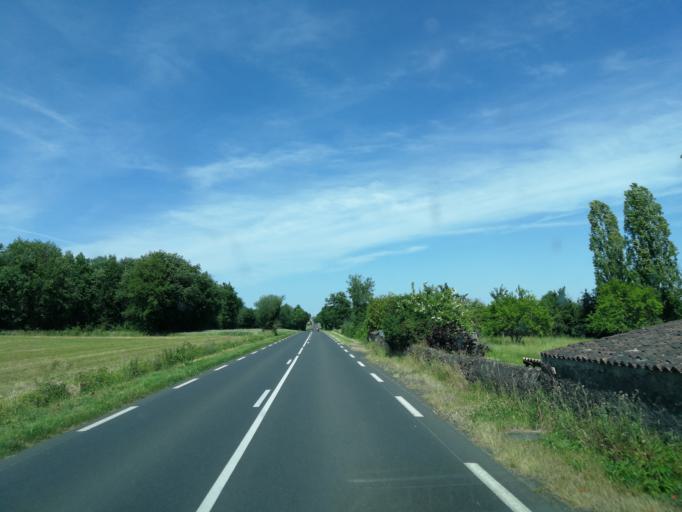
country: FR
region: Poitou-Charentes
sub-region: Departement des Deux-Sevres
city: Saint-Jean-de-Thouars
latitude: 46.9410
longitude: -0.2383
